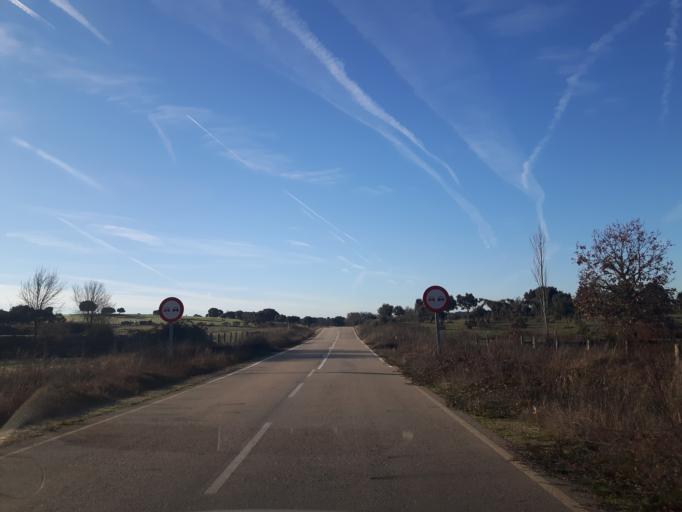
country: ES
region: Castille and Leon
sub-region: Provincia de Salamanca
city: Olmedo de Camaces
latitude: 40.8928
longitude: -6.6213
